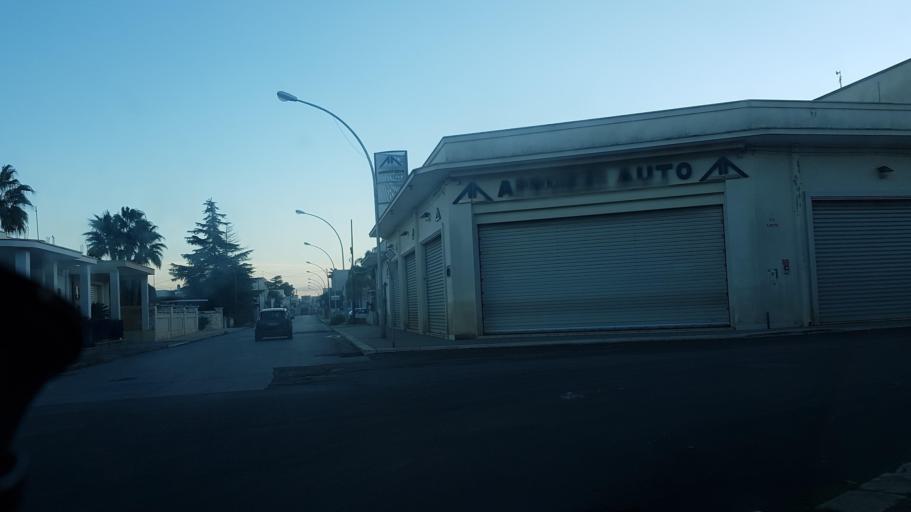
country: IT
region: Apulia
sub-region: Provincia di Brindisi
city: San Michele Salentino
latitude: 40.6358
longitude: 17.6321
